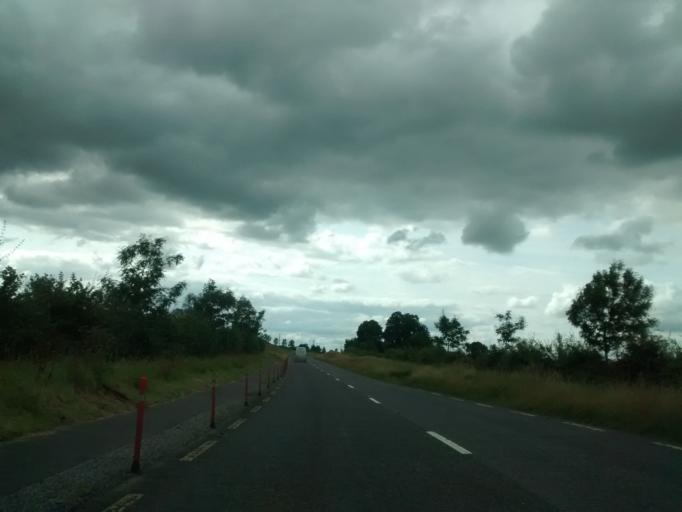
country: IE
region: Leinster
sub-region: An Iarmhi
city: Moate
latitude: 53.3818
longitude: -7.6711
